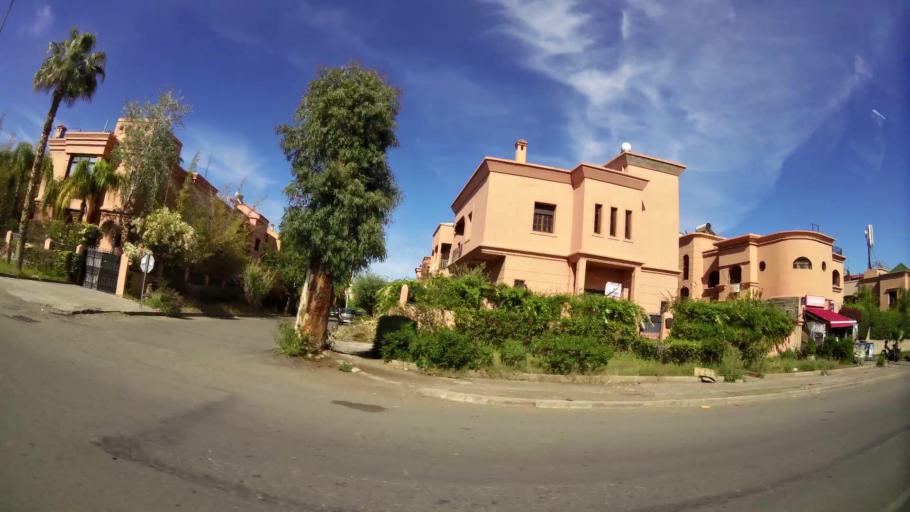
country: MA
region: Marrakech-Tensift-Al Haouz
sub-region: Marrakech
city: Marrakesh
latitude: 31.6509
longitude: -8.0494
